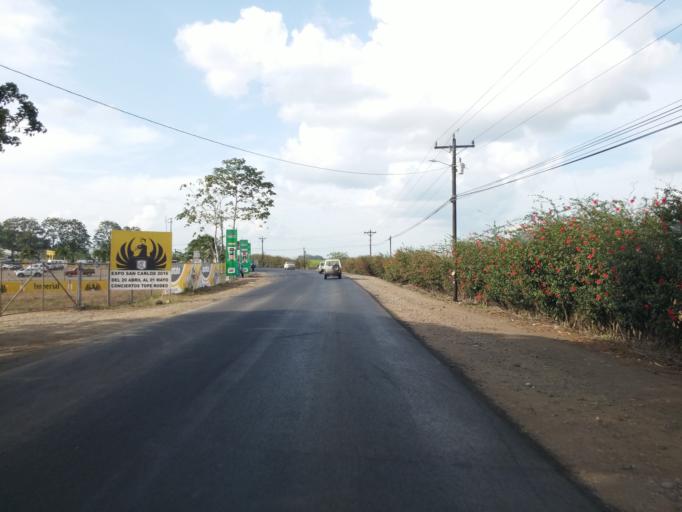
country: CR
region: Alajuela
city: Quesada
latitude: 10.4396
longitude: -84.4660
